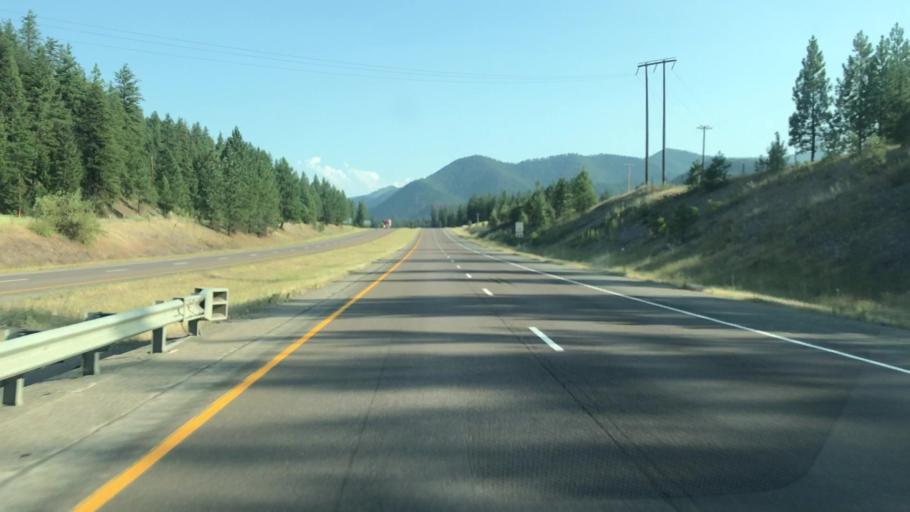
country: US
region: Montana
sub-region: Mineral County
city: Superior
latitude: 47.0665
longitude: -114.7644
